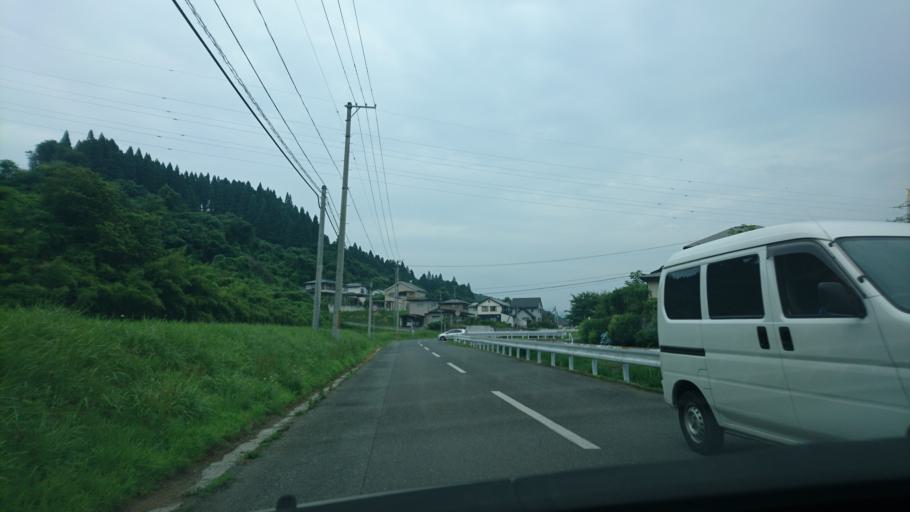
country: JP
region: Iwate
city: Ichinoseki
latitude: 38.9079
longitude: 141.1191
